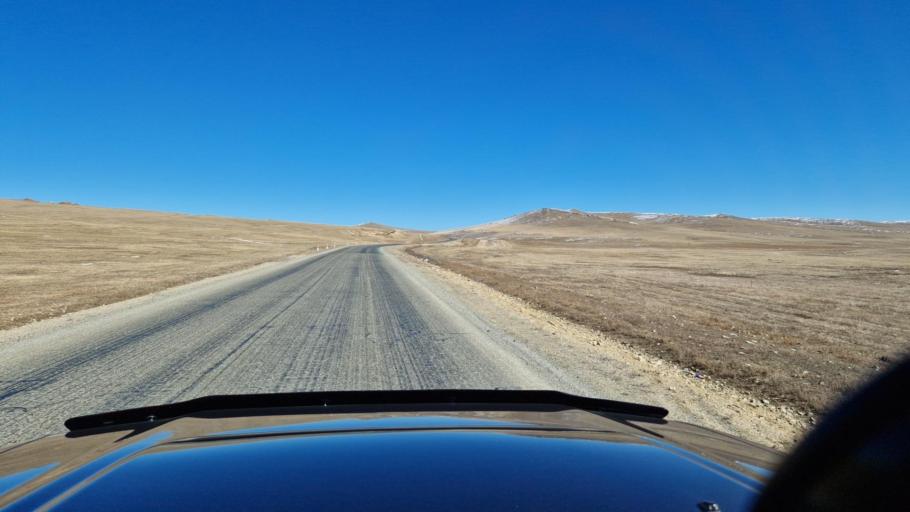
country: MN
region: Hentiy
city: Modot
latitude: 47.7944
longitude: 108.6868
